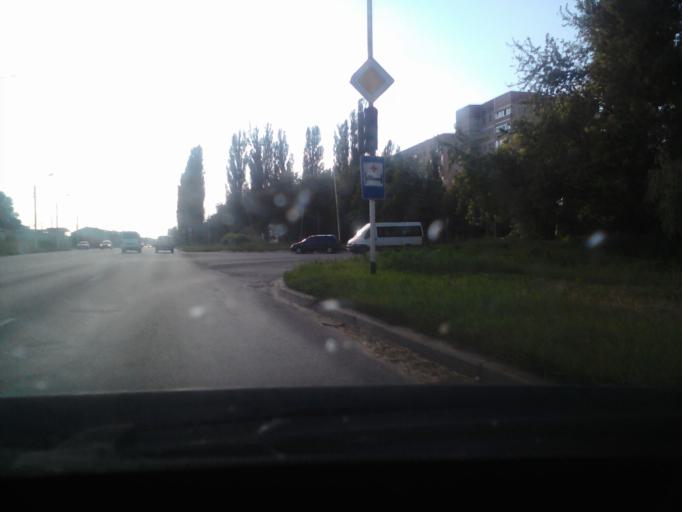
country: RU
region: Kursk
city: Kurchatov
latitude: 51.6538
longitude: 35.6738
